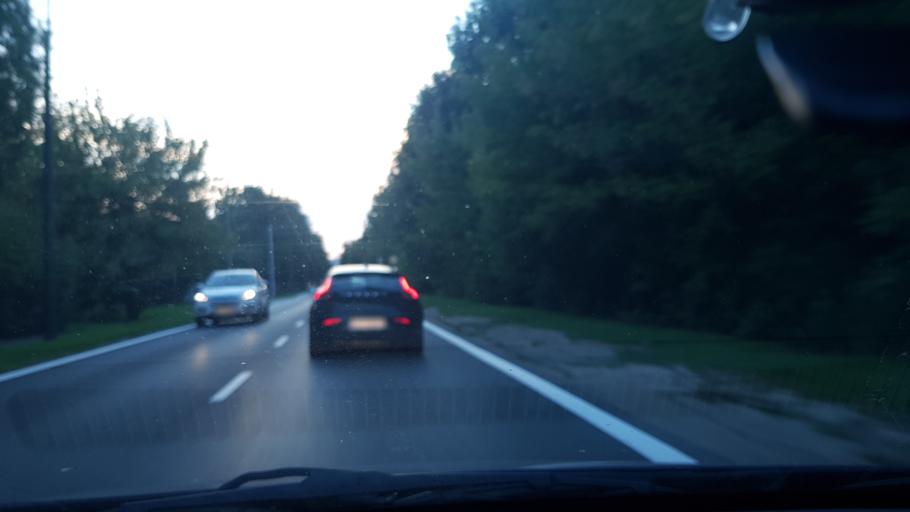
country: PL
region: Masovian Voivodeship
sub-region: Warszawa
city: Targowek
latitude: 52.2919
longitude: 21.0673
